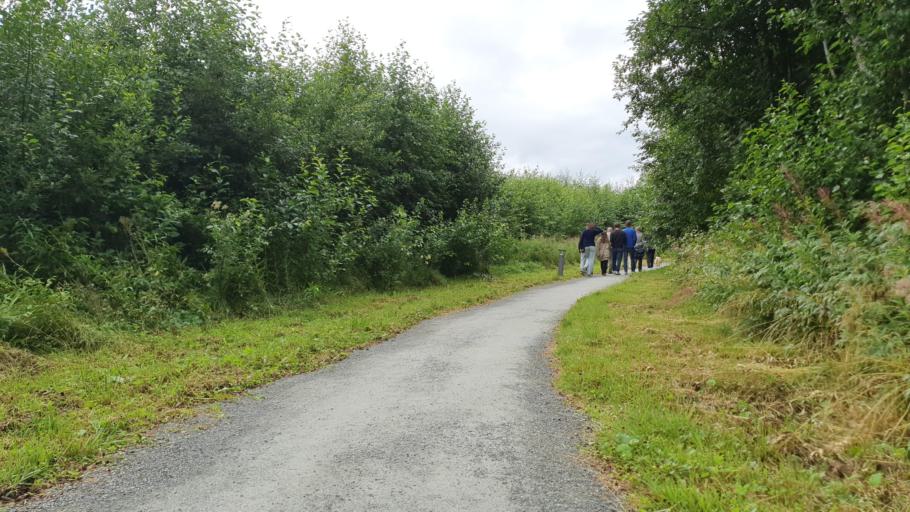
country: NO
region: Sor-Trondelag
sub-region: Selbu
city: Mebonden
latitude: 63.2309
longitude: 11.0237
